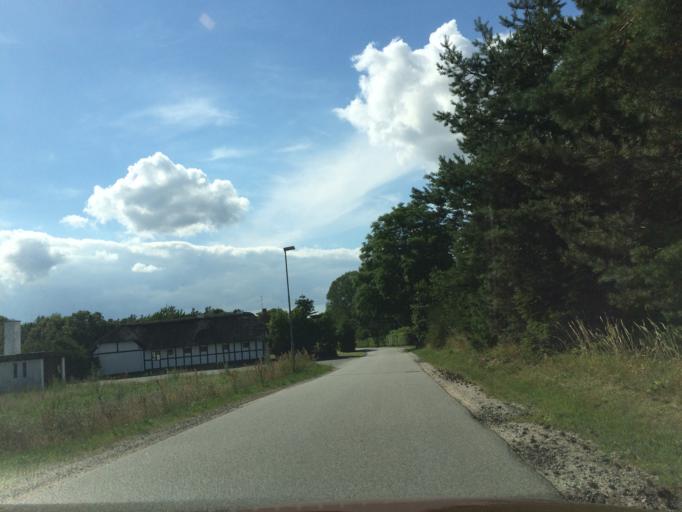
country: DK
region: Central Jutland
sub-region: Syddjurs Kommune
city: Ebeltoft
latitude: 56.2858
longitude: 10.7190
